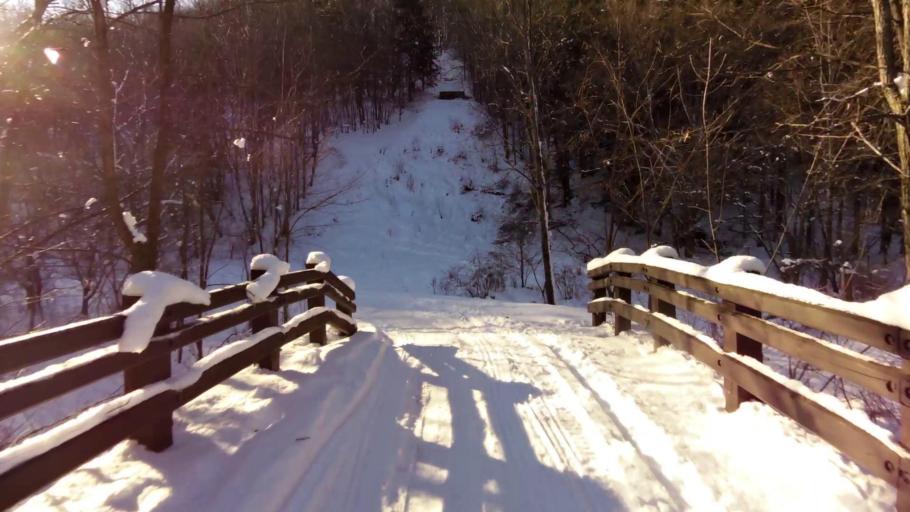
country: US
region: New York
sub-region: Cattaraugus County
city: Salamanca
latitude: 42.1055
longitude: -78.7513
